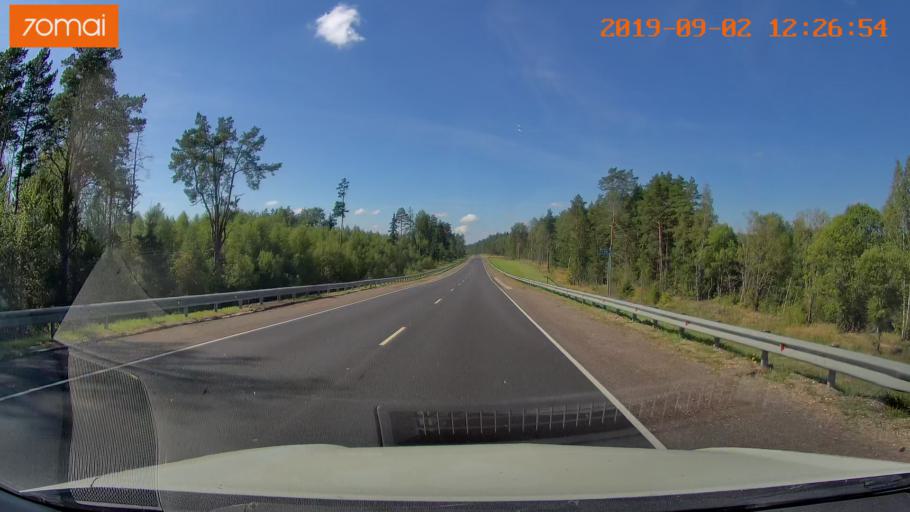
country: RU
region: Smolensk
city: Shumyachi
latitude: 53.8552
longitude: 32.5576
